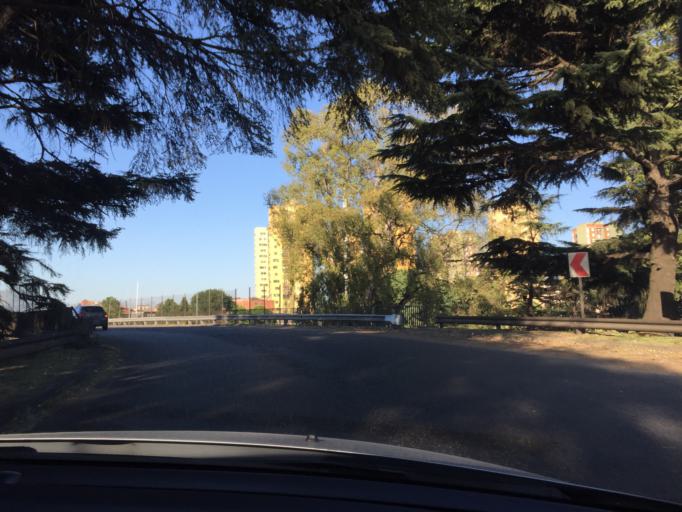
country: AR
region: Buenos Aires F.D.
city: Villa Lugano
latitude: -34.6855
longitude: -58.4863
